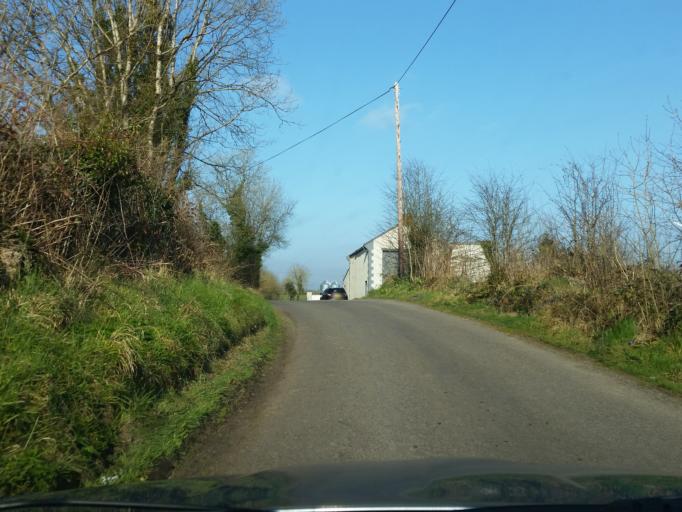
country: IE
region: Ulster
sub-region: County Monaghan
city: Clones
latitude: 54.2303
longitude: -7.2290
